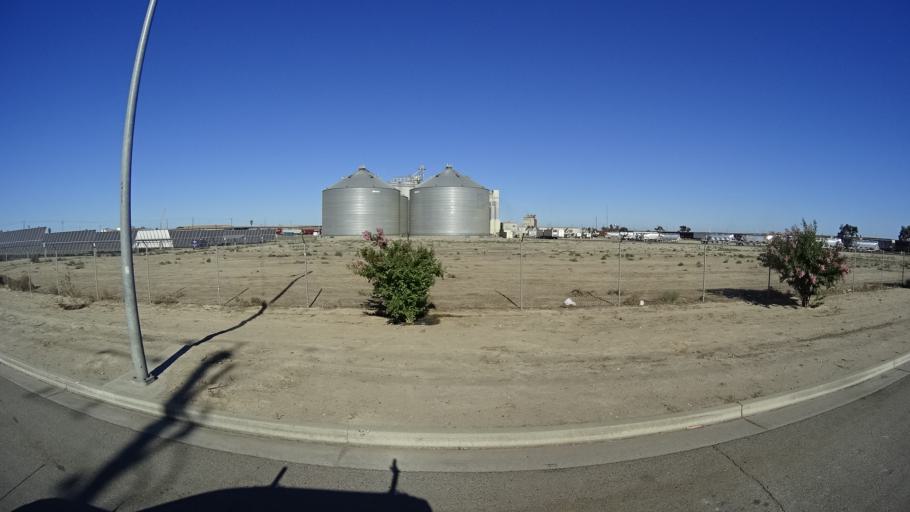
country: US
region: California
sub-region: Fresno County
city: Fresno
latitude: 36.6945
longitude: -119.7458
